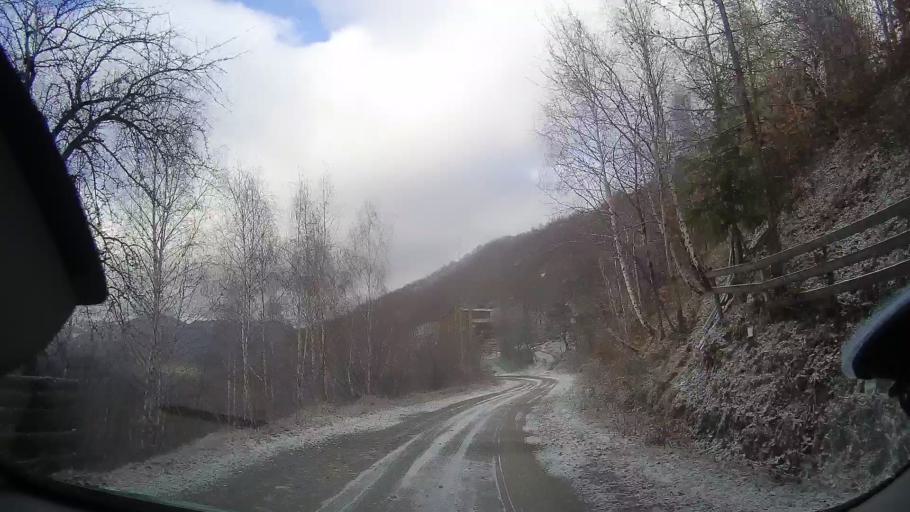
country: RO
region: Cluj
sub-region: Comuna Valea Ierii
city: Valea Ierii
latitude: 46.6746
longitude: 23.3208
